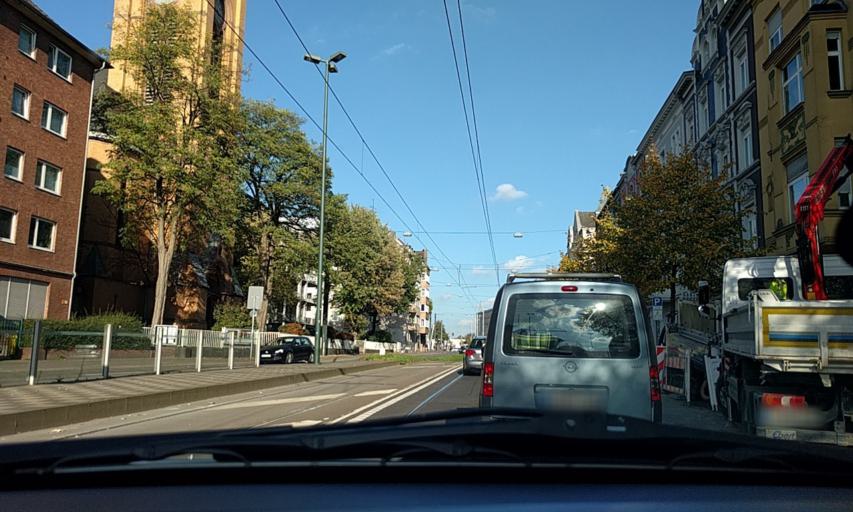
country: DE
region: North Rhine-Westphalia
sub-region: Regierungsbezirk Dusseldorf
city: Dusseldorf
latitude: 51.2149
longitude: 6.8012
